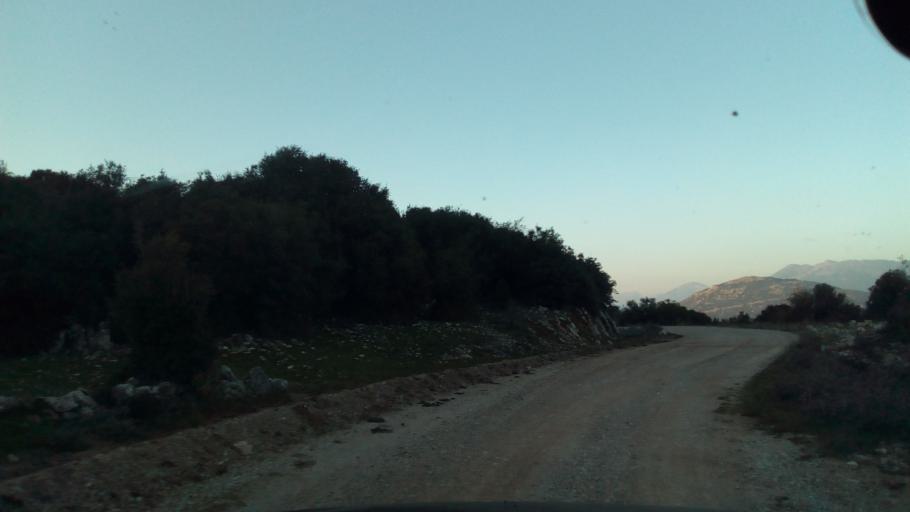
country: GR
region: West Greece
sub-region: Nomos Aitolias kai Akarnanias
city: Nafpaktos
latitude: 38.4665
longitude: 21.8254
